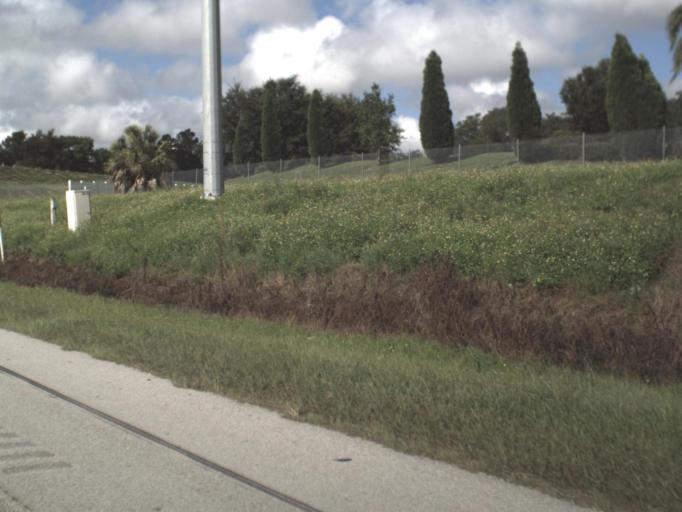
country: US
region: Florida
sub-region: Polk County
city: Gibsonia
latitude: 28.1110
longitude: -81.9420
